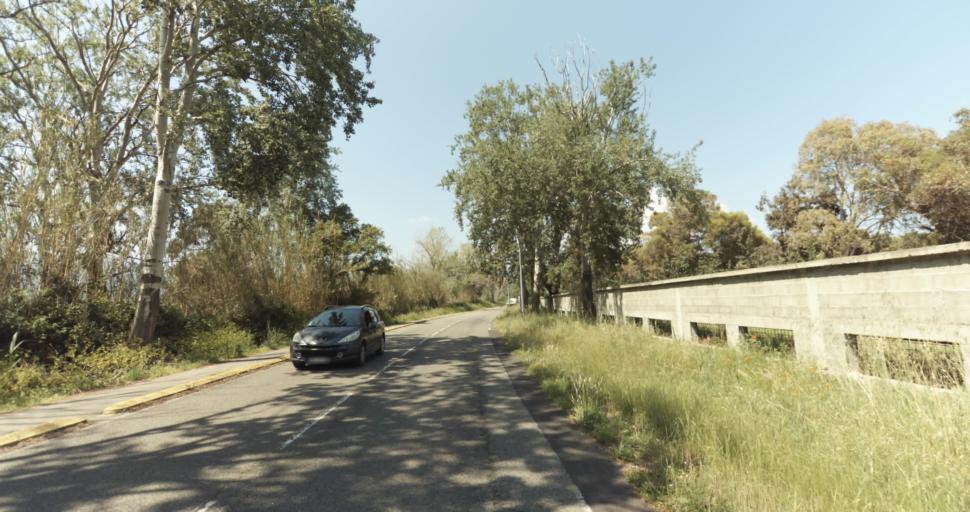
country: FR
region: Corsica
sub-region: Departement de la Haute-Corse
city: Biguglia
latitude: 42.6251
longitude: 9.4698
